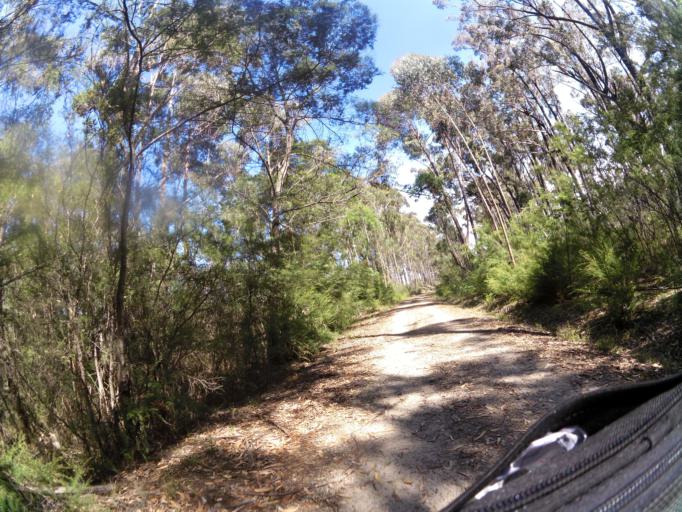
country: AU
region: Victoria
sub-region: East Gippsland
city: Lakes Entrance
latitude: -37.7224
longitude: 148.1478
